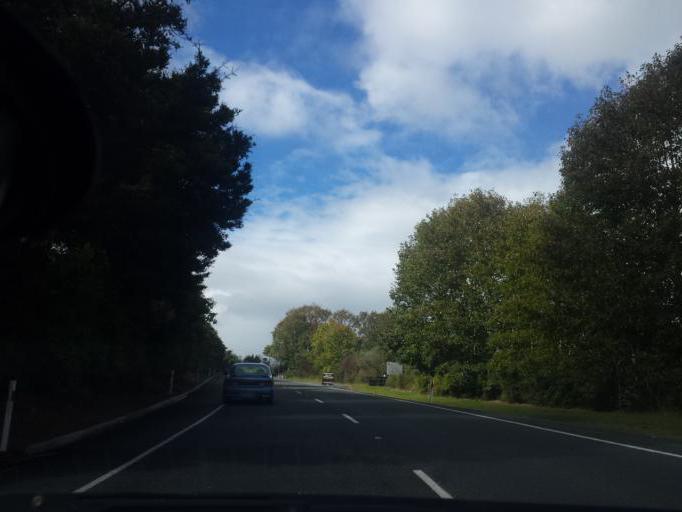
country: NZ
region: Auckland
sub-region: Auckland
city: Warkworth
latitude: -36.3985
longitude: 174.7042
